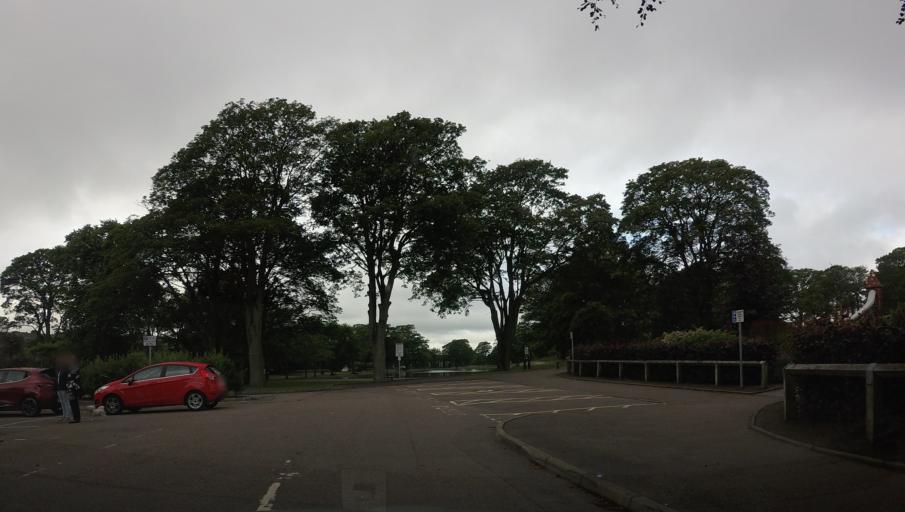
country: GB
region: Scotland
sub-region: Aberdeen City
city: Aberdeen
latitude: 57.1299
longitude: -2.0993
